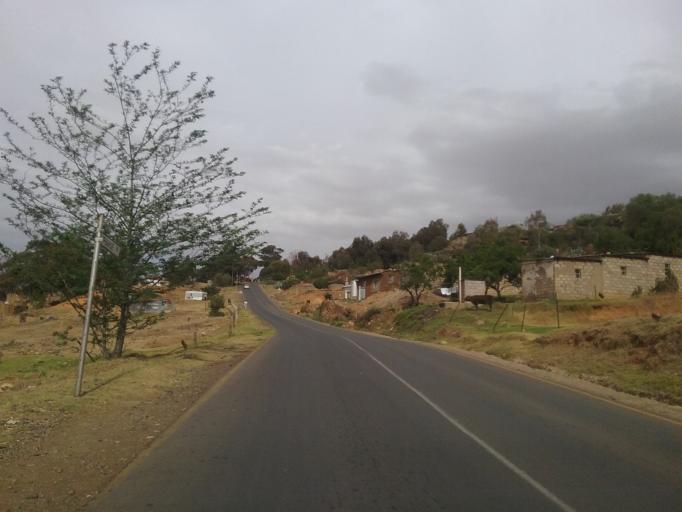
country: LS
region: Quthing
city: Quthing
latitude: -30.4028
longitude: 27.7031
